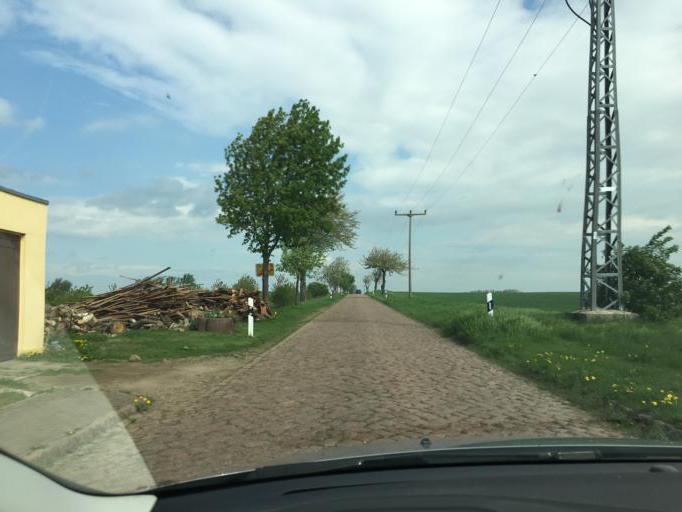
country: DE
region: Saxony-Anhalt
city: Grobzig
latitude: 51.6469
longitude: 11.8442
